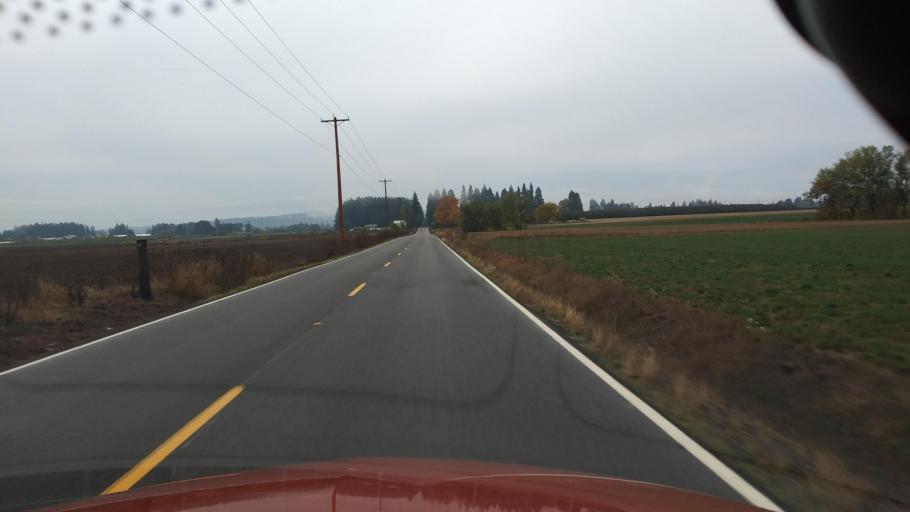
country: US
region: Oregon
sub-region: Washington County
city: Forest Grove
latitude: 45.5460
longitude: -123.0870
